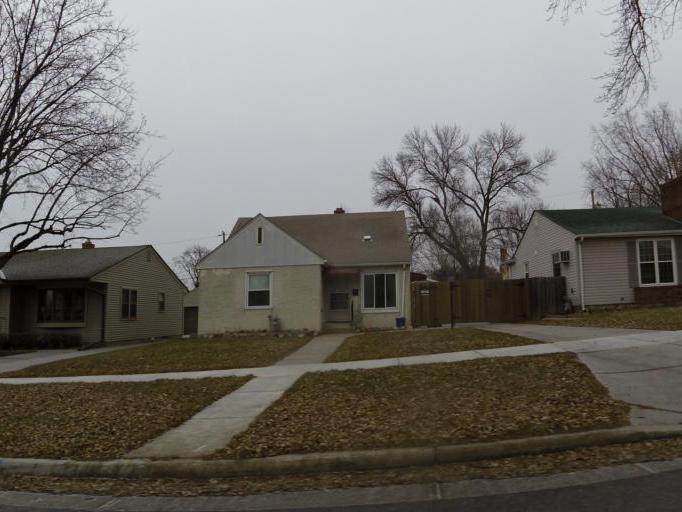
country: US
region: Minnesota
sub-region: Ramsey County
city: Maplewood
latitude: 44.9568
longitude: -93.0290
